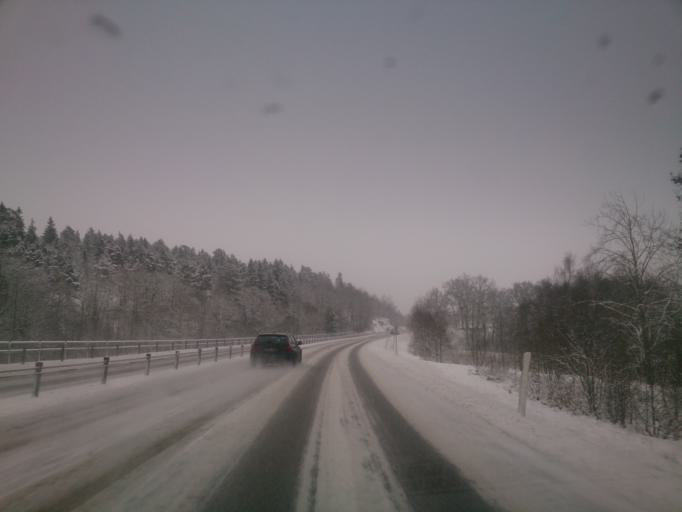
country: SE
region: OEstergoetland
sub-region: Norrkopings Kommun
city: Svartinge
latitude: 58.6994
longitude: 15.8979
